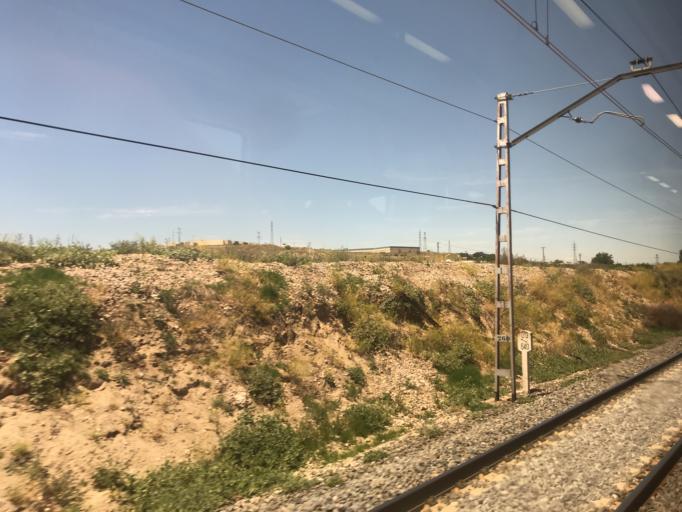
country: ES
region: Madrid
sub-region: Provincia de Madrid
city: Aranjuez
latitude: 40.0892
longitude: -3.6312
